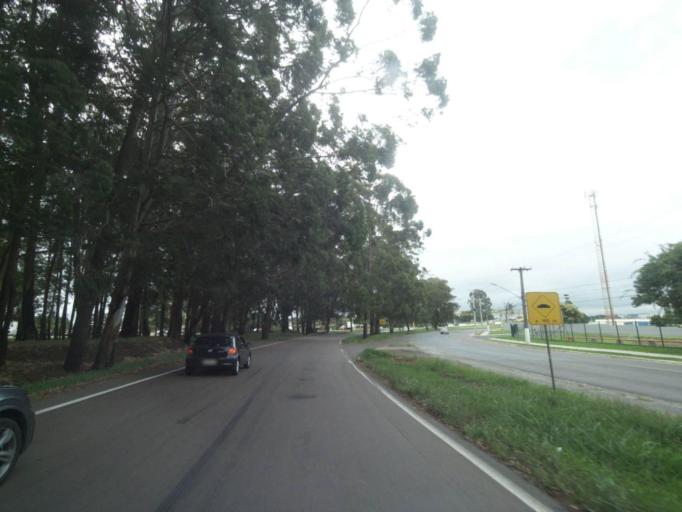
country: BR
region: Parana
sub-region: Sao Jose Dos Pinhais
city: Sao Jose dos Pinhais
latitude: -25.5377
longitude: -49.3124
